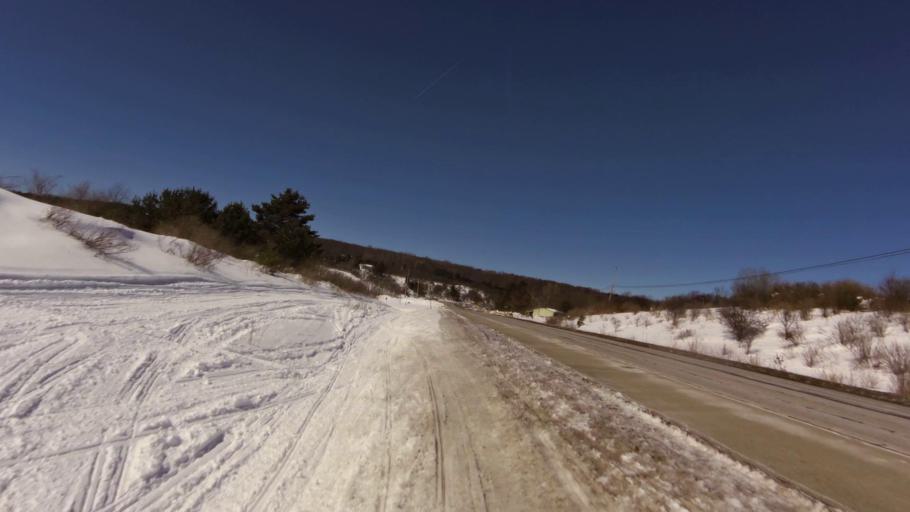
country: US
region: New York
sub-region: Wyoming County
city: Arcade
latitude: 42.4411
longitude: -78.3360
